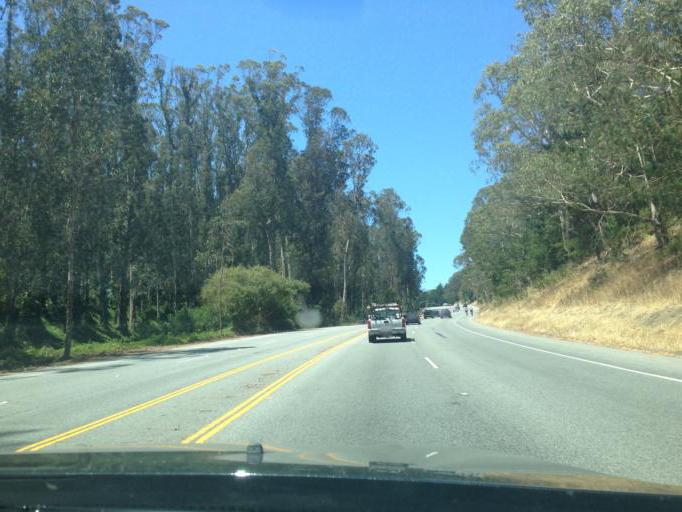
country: US
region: California
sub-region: San Mateo County
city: Pacifica
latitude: 37.6280
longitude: -122.4504
